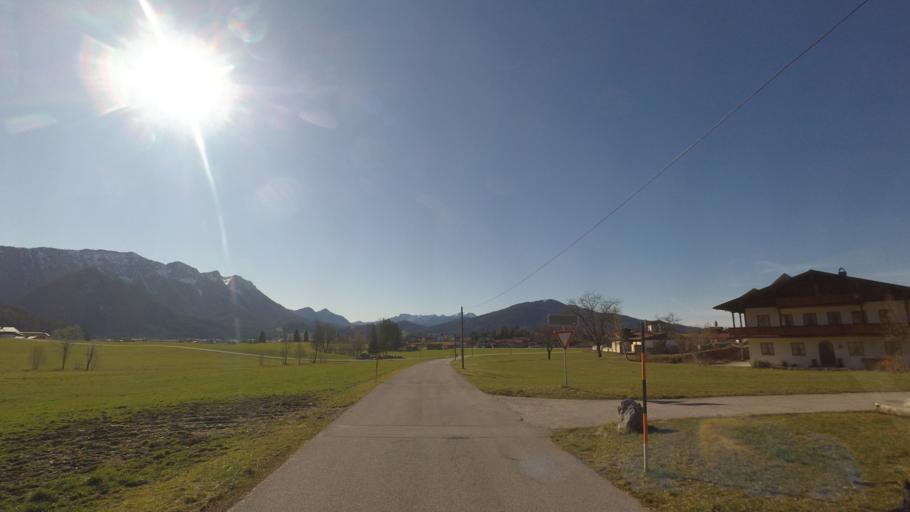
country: DE
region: Bavaria
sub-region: Upper Bavaria
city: Inzell
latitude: 47.7683
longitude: 12.7723
